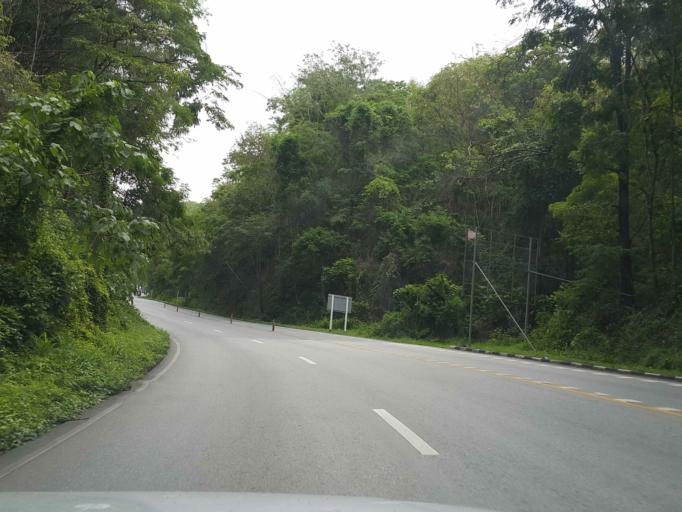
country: TH
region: Tak
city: Tak
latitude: 16.8091
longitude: 98.9587
